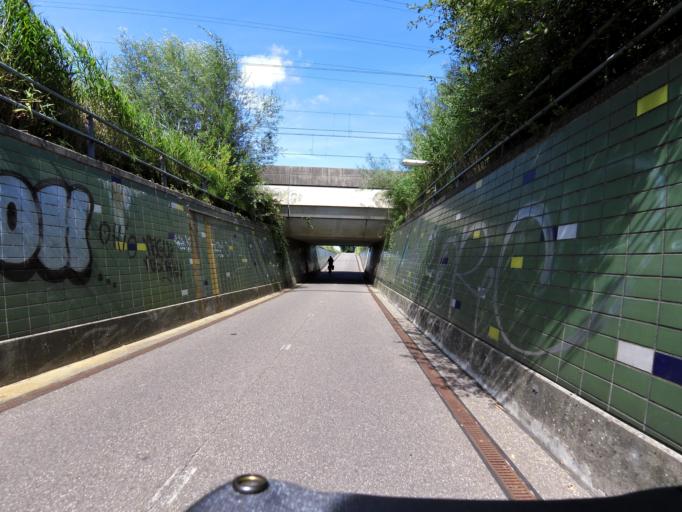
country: NL
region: South Holland
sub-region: Gemeente Barendrecht
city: Barendrecht
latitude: 51.8655
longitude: 4.5291
